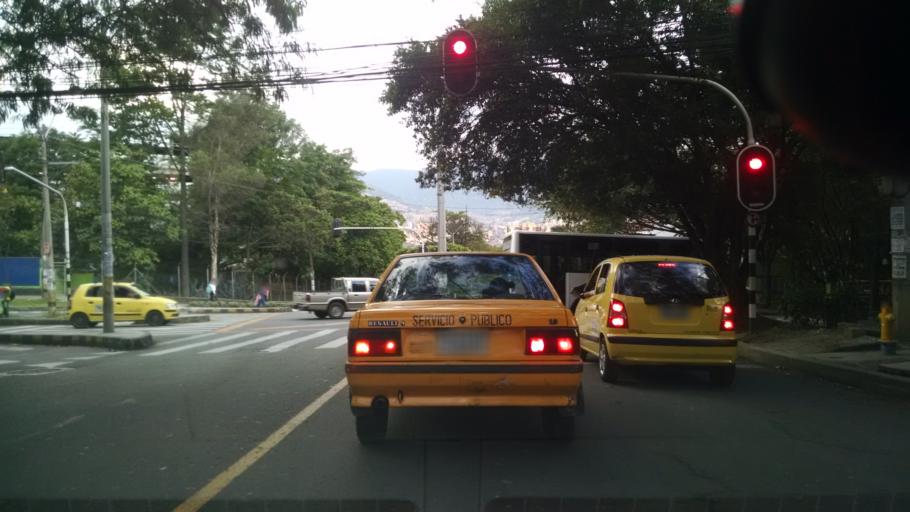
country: CO
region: Antioquia
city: Medellin
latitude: 6.2774
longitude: -75.5816
